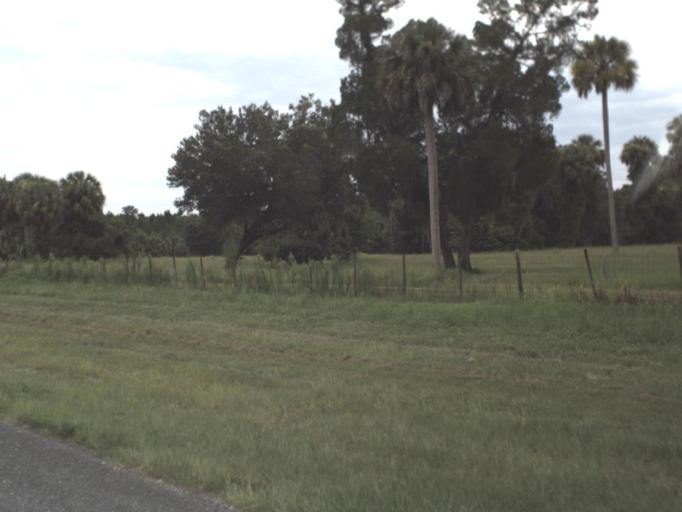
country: US
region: Florida
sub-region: Citrus County
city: Inverness
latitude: 28.8512
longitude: -82.2325
